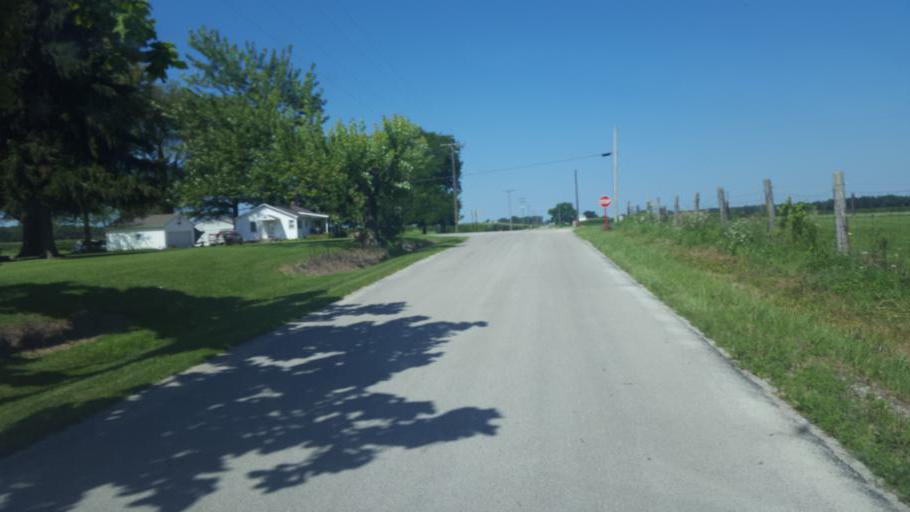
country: US
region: Ohio
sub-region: Morrow County
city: Cardington
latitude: 40.4518
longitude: -82.9050
